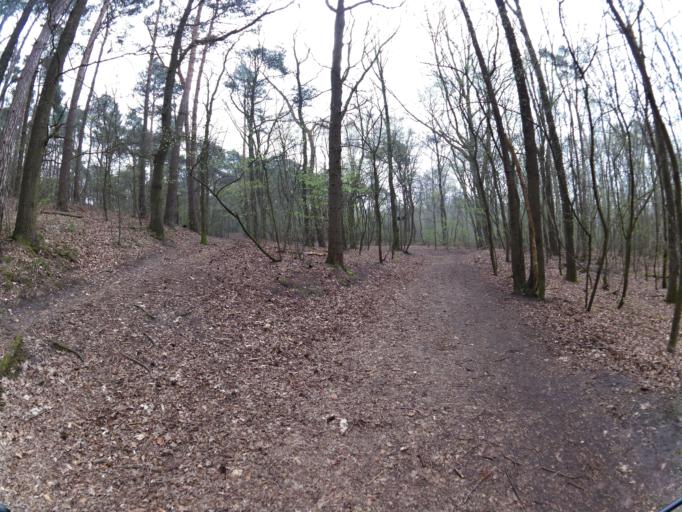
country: NL
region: Limburg
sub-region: Gemeente Onderbanken
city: Schinveld
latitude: 50.9602
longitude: 5.9830
